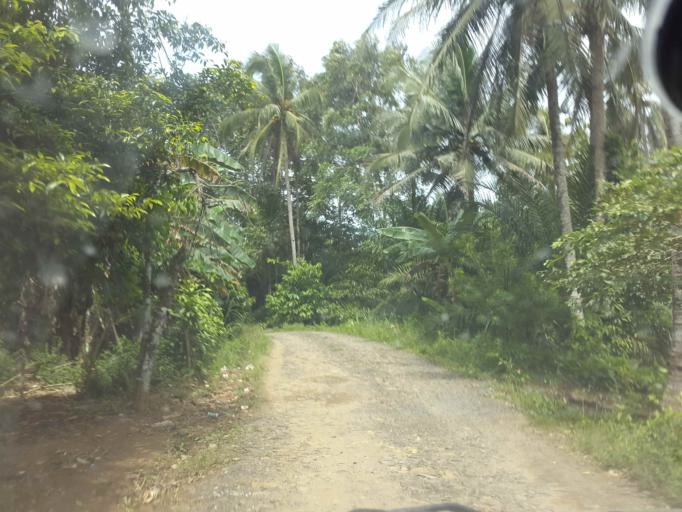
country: ID
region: Lampung
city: Sidorejo
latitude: -5.5572
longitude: 105.4561
